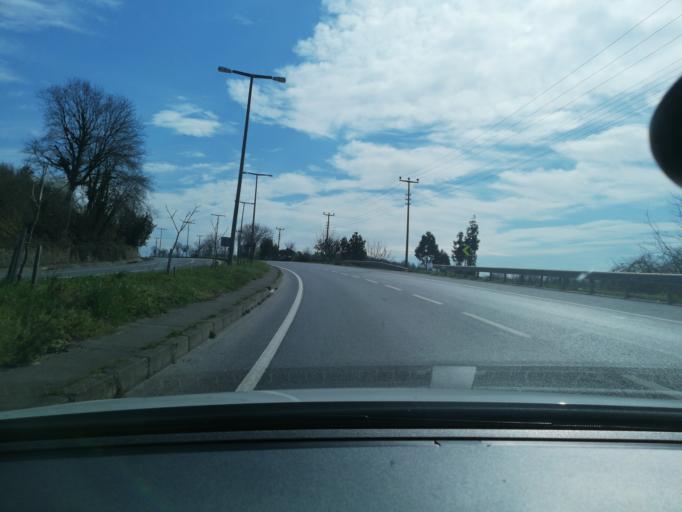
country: TR
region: Duzce
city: Akcakoca
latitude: 41.0836
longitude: 31.1566
